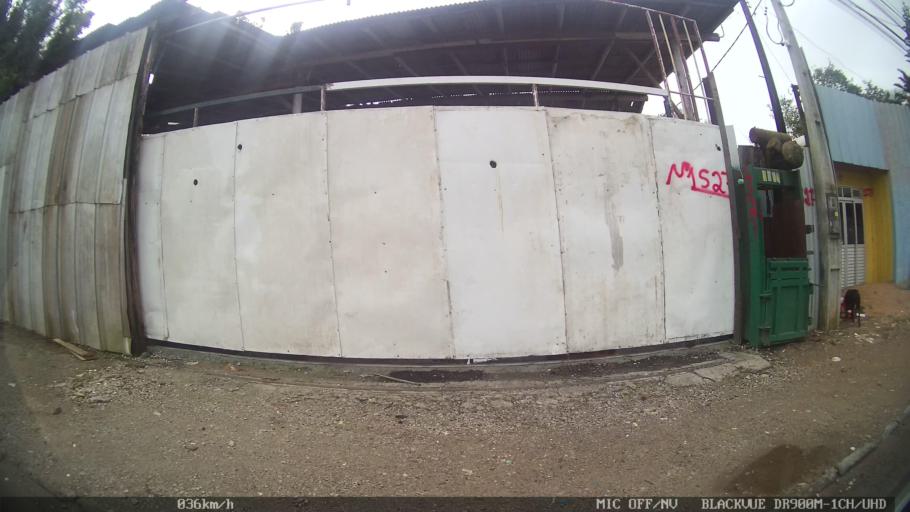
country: BR
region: Santa Catarina
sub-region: Biguacu
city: Biguacu
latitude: -27.5085
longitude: -48.6482
